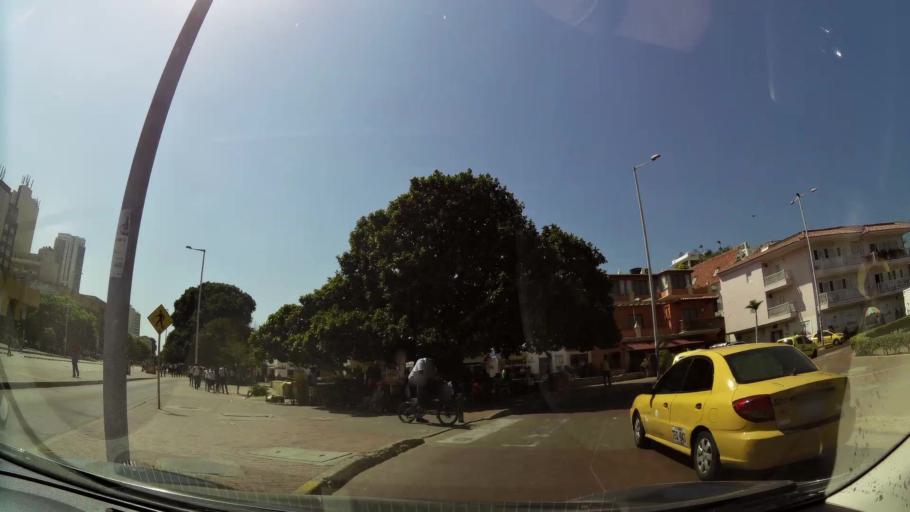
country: CO
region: Bolivar
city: Cartagena
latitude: 10.4265
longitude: -75.5449
